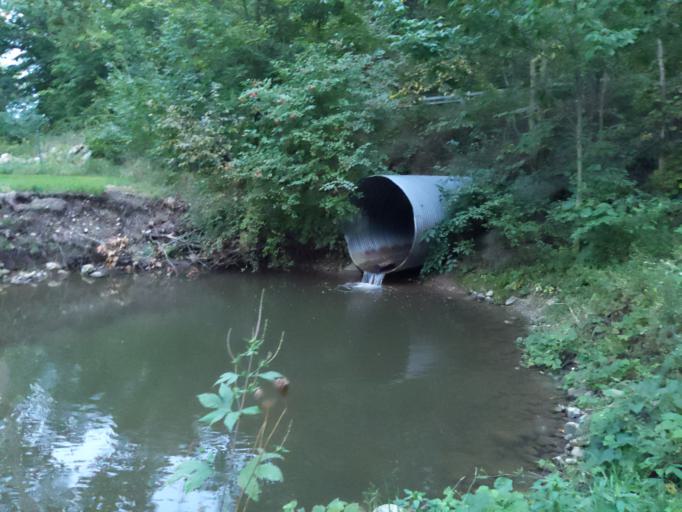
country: US
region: Michigan
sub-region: Ionia County
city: Portland
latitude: 42.8875
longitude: -84.9311
